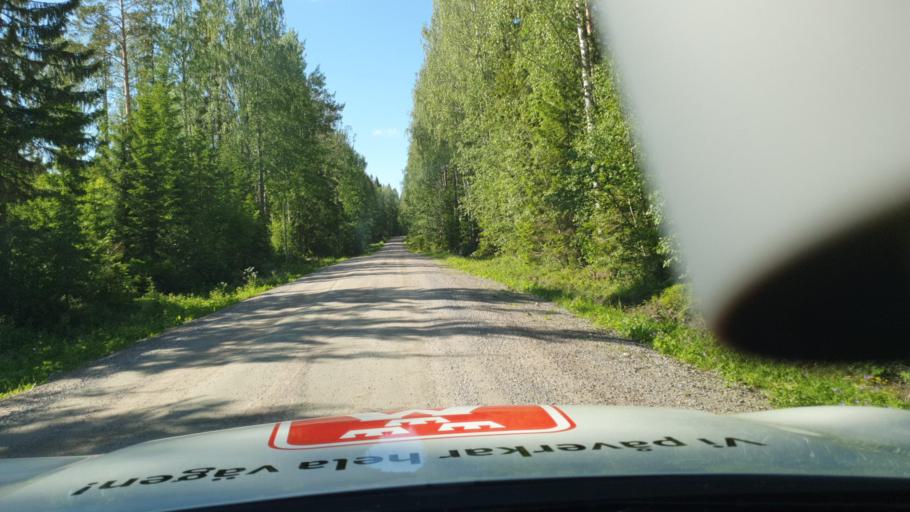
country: SE
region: Vaesterbotten
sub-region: Vannas Kommun
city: Vaennaes
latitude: 63.7845
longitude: 19.6286
